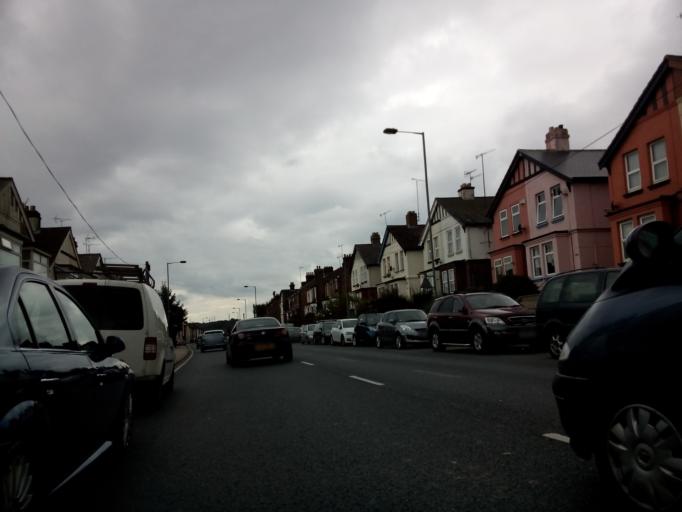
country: GB
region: England
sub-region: Suffolk
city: Ipswich
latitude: 52.0420
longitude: 1.1527
